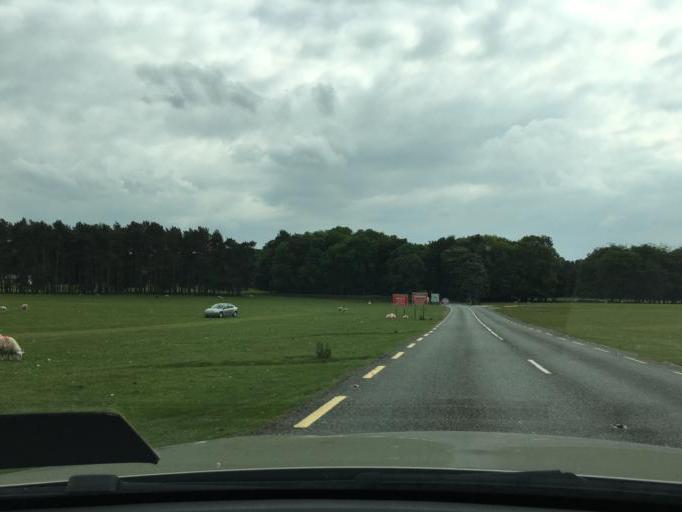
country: IE
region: Leinster
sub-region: Kildare
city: Athgarvan
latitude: 53.1529
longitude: -6.8304
